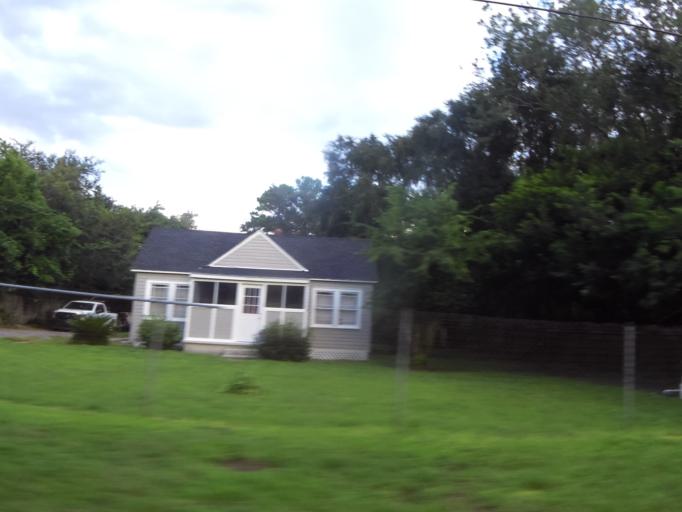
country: US
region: Florida
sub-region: Duval County
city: Jacksonville
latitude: 30.3194
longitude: -81.7759
